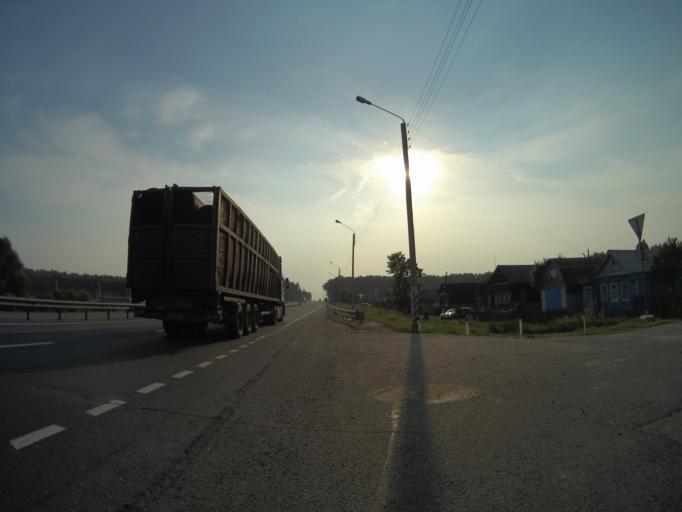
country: RU
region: Vladimir
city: Melekhovo
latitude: 56.2082
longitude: 41.2373
